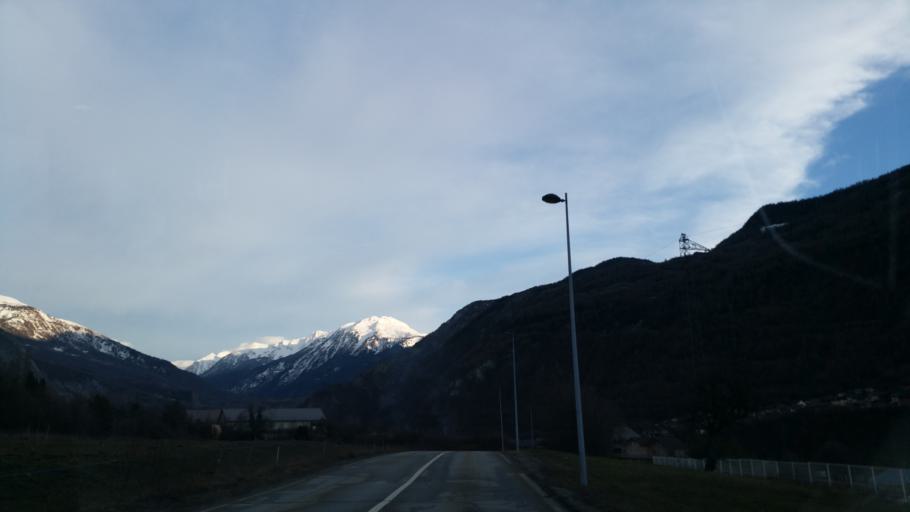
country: FR
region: Rhone-Alpes
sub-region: Departement de la Savoie
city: Villargondran
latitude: 45.2562
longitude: 6.3975
